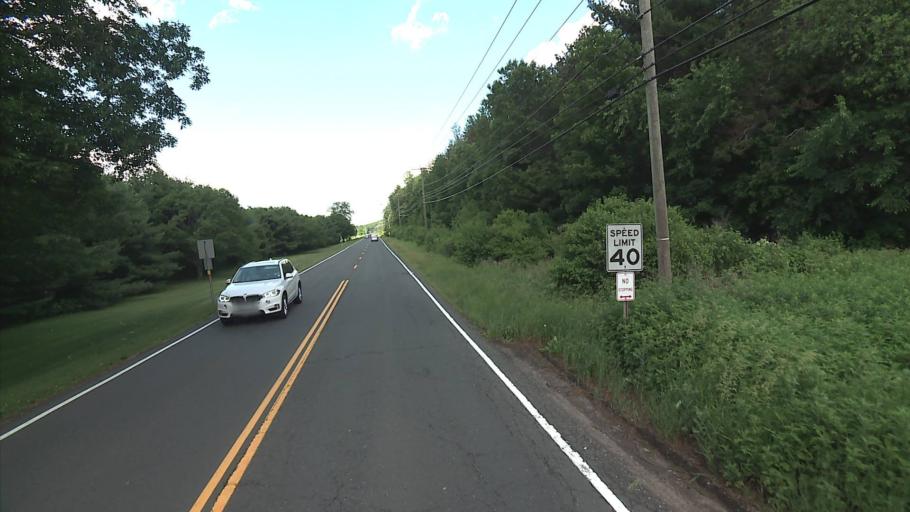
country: US
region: Connecticut
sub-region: Hartford County
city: Hazardville
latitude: 42.0172
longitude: -72.5140
